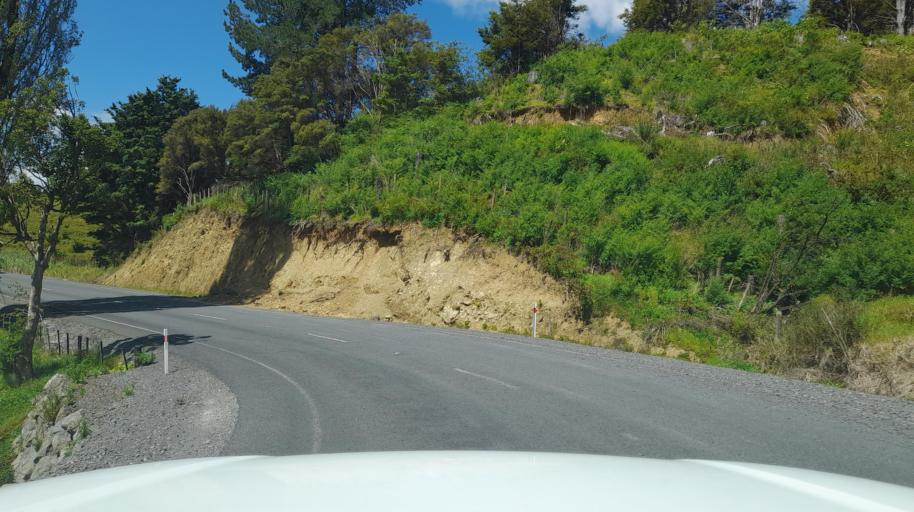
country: NZ
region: Northland
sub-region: Far North District
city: Taipa
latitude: -35.1091
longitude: 173.4448
